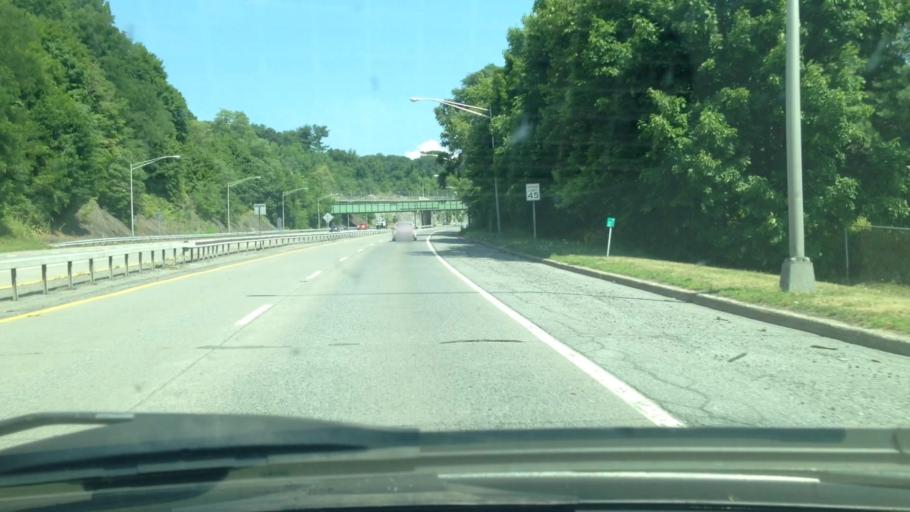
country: US
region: New York
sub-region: Ulster County
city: Kingston
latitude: 41.9239
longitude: -73.9852
